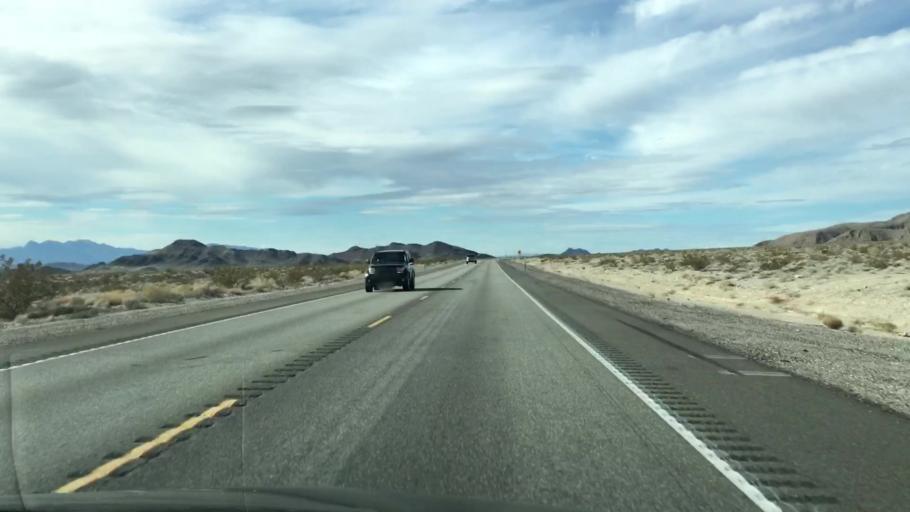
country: US
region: Nevada
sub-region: Nye County
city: Pahrump
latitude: 36.5724
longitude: -116.1757
